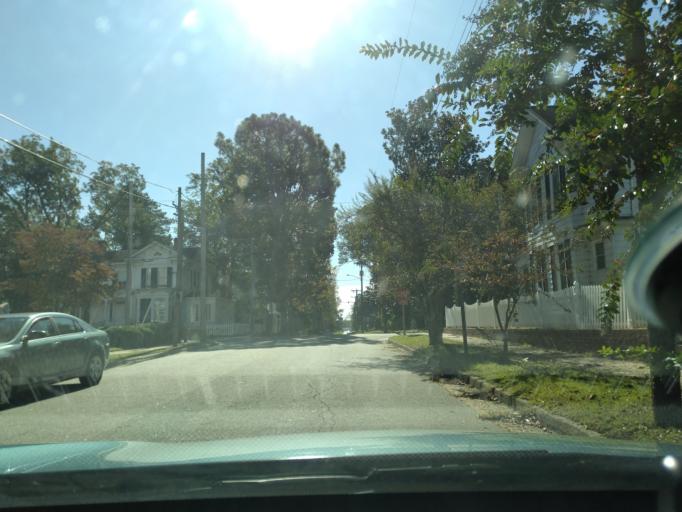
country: US
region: North Carolina
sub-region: Washington County
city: Plymouth
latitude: 35.8669
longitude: -76.7491
